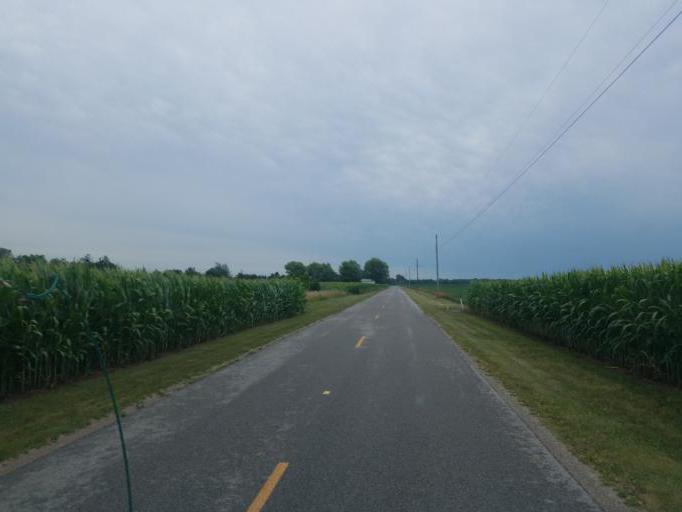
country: US
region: Ohio
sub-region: Paulding County
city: Antwerp
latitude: 41.2372
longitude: -84.7379
